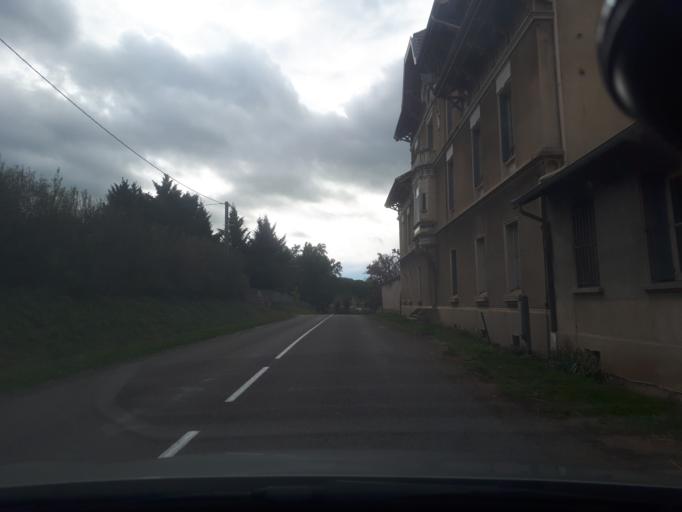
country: FR
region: Rhone-Alpes
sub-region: Departement de la Loire
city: Bellegarde-en-Forez
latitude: 45.6908
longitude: 4.3029
